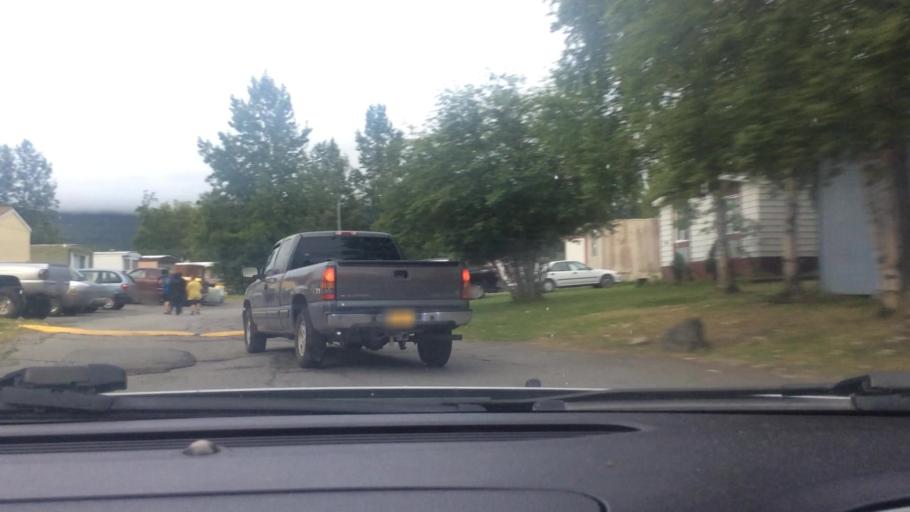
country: US
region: Alaska
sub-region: Anchorage Municipality
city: Elmendorf Air Force Base
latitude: 61.2001
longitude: -149.7287
